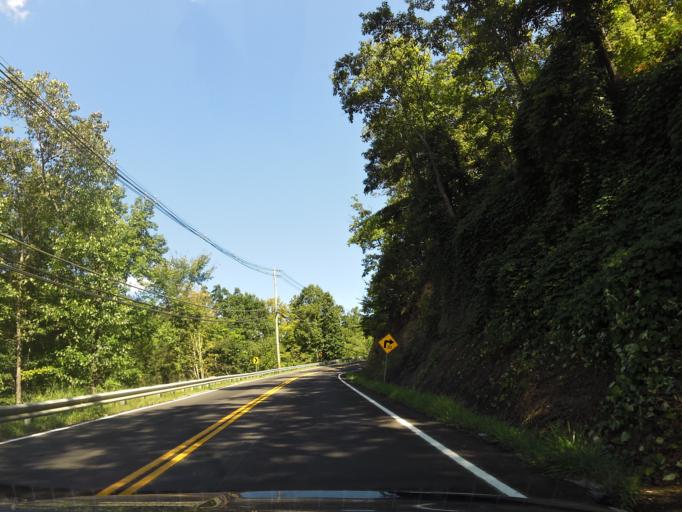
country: US
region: Kentucky
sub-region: Clay County
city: Manchester
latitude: 37.0964
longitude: -83.6681
